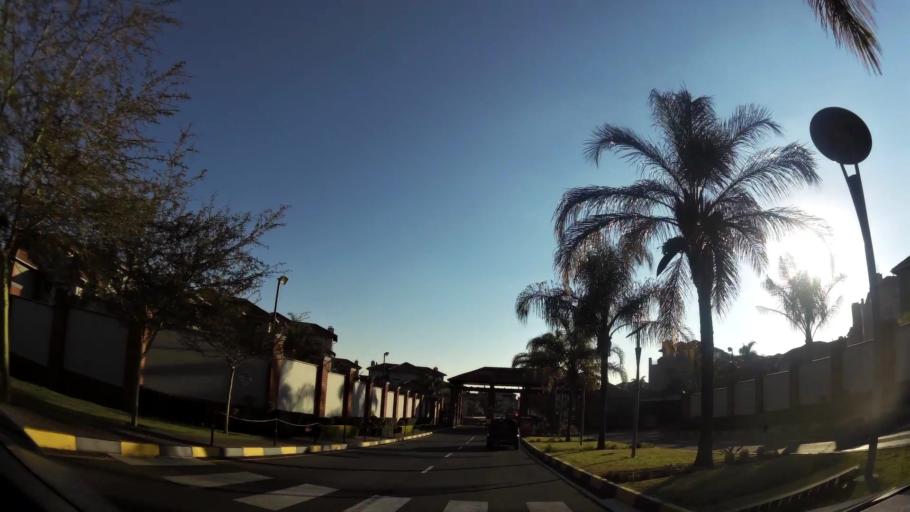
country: ZA
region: Gauteng
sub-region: Ekurhuleni Metropolitan Municipality
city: Germiston
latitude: -26.1724
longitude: 28.1619
